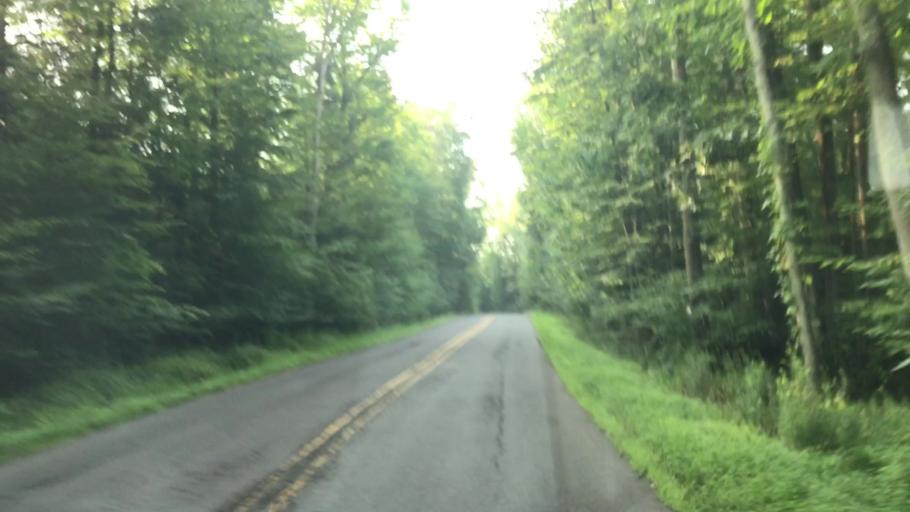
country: US
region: Pennsylvania
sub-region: Wyoming County
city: Factoryville
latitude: 41.6133
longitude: -75.7413
